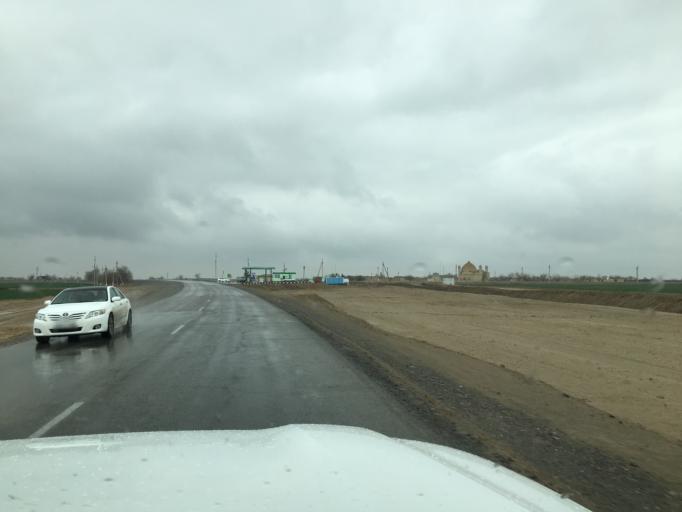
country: TM
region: Mary
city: Bayramaly
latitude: 37.4076
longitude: 62.1710
